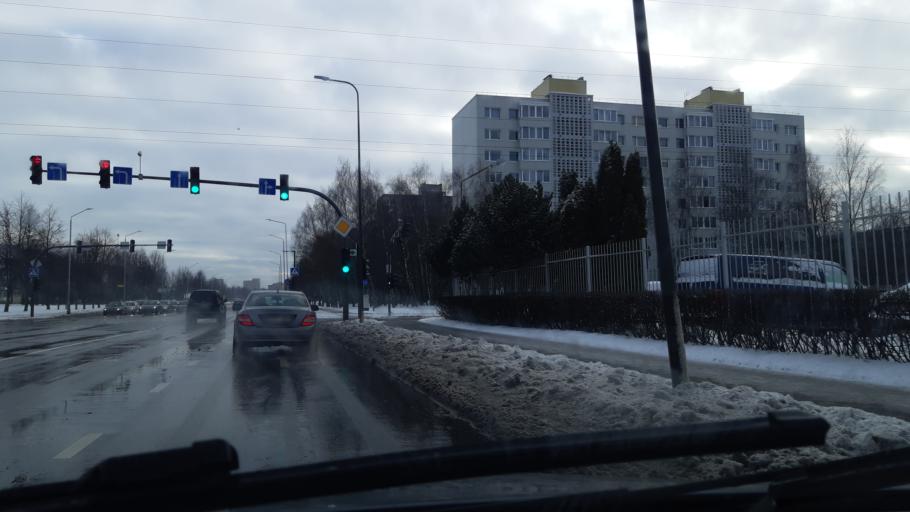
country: LT
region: Kauno apskritis
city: Dainava (Kaunas)
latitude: 54.9270
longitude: 23.9737
